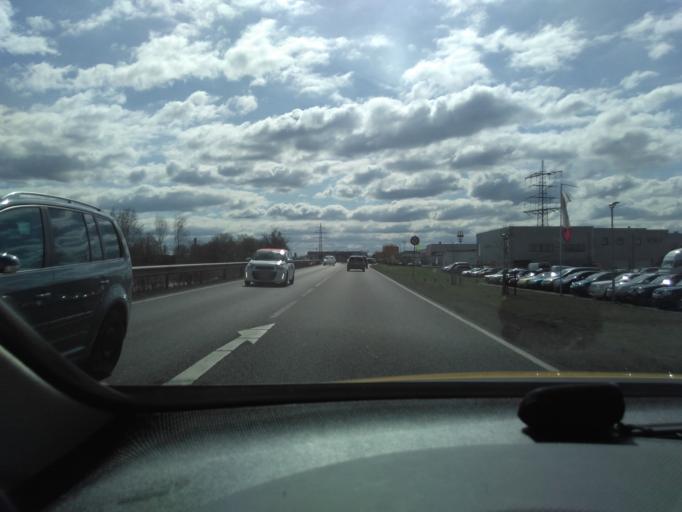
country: DE
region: North Rhine-Westphalia
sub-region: Regierungsbezirk Koln
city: Erftstadt
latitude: 50.7982
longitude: 6.7832
